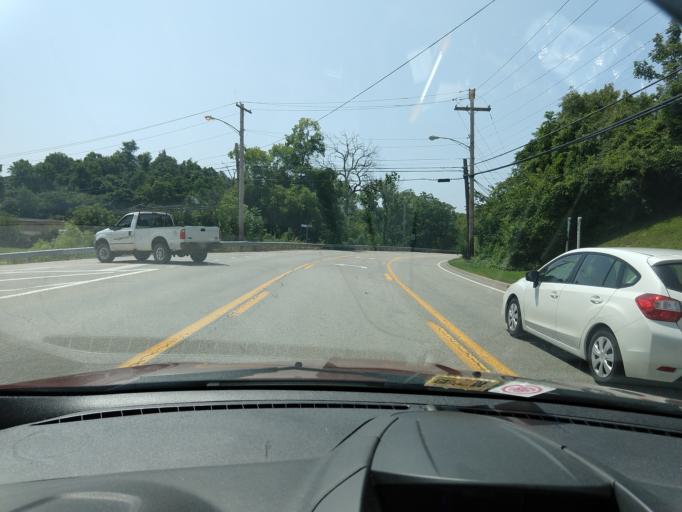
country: US
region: West Virginia
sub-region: Harrison County
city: Clarksburg
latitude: 39.2711
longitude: -80.3699
